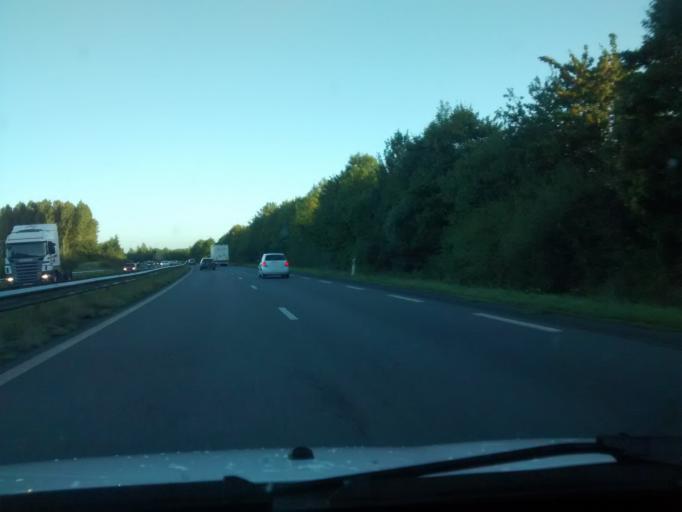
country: FR
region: Brittany
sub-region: Departement d'Ille-et-Vilaine
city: Vignoc
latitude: 48.2677
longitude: -1.7813
